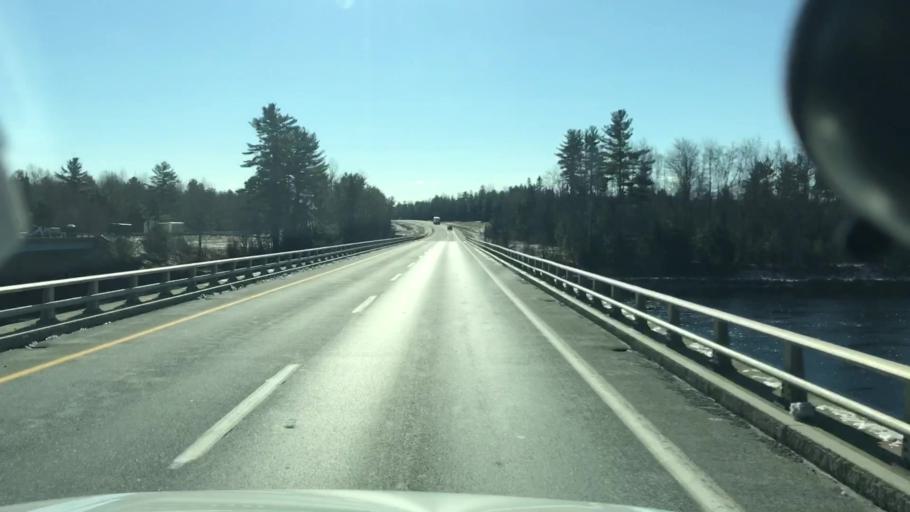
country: US
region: Maine
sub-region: Penobscot County
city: Howland
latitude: 45.2662
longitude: -68.6803
